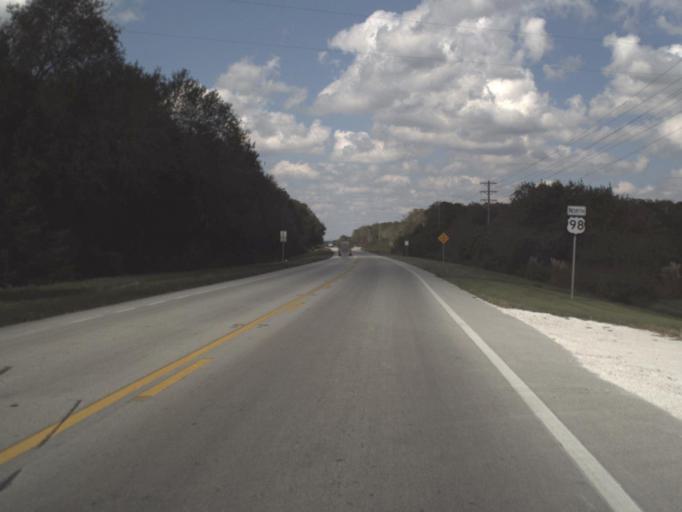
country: US
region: Florida
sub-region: Okeechobee County
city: Okeechobee
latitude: 27.3762
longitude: -80.9842
